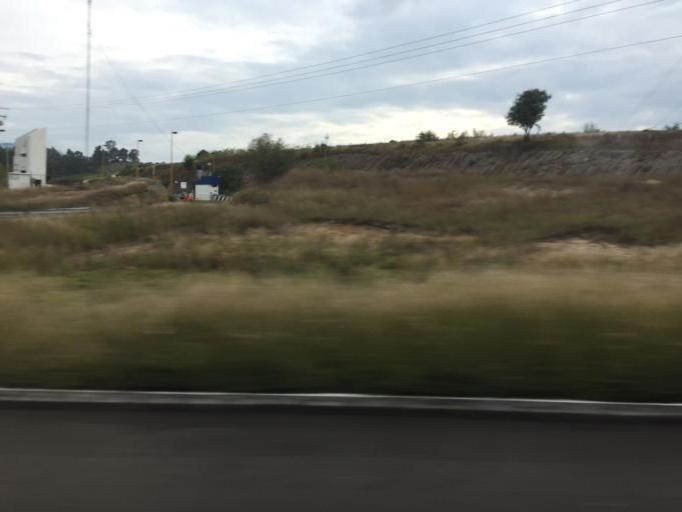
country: MX
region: Mexico
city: Huaniqueo de Morales
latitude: 19.8836
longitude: -101.5115
